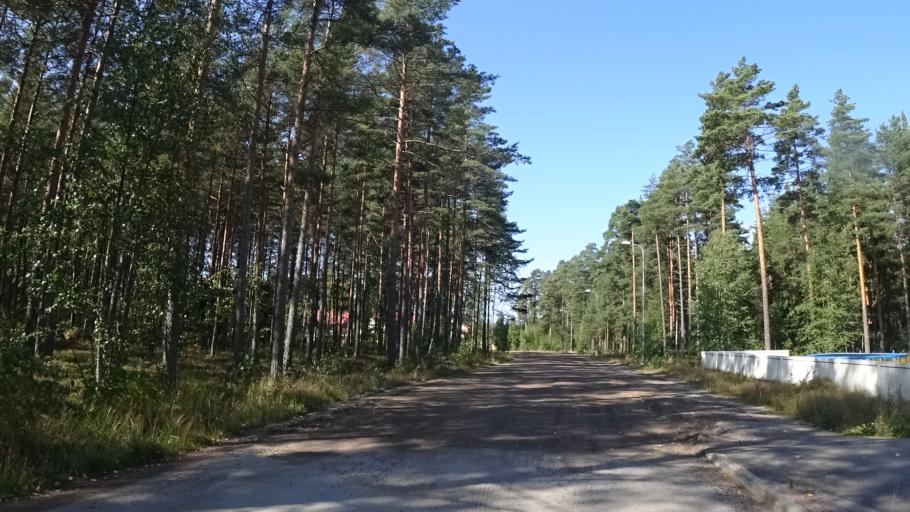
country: FI
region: Kymenlaakso
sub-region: Kotka-Hamina
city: Hamina
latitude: 60.5385
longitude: 27.2295
